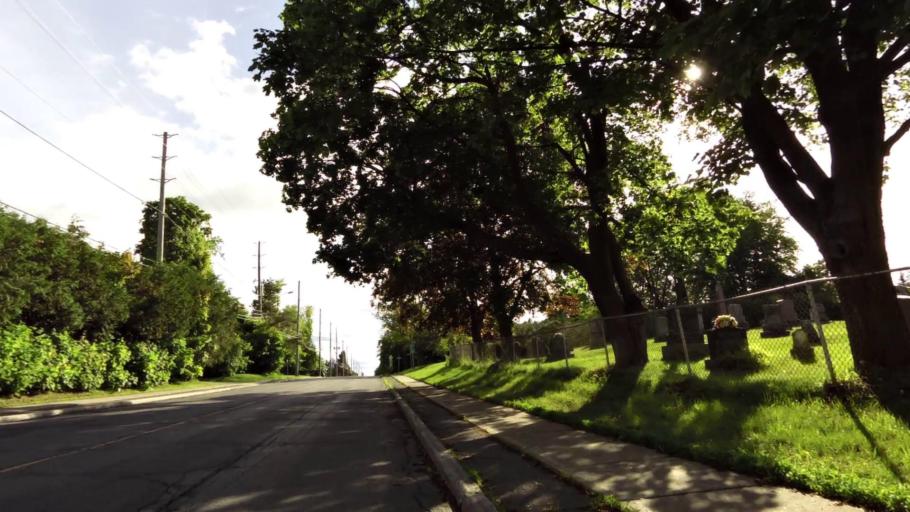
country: CA
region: Ontario
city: Ottawa
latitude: 45.2622
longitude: -75.5619
